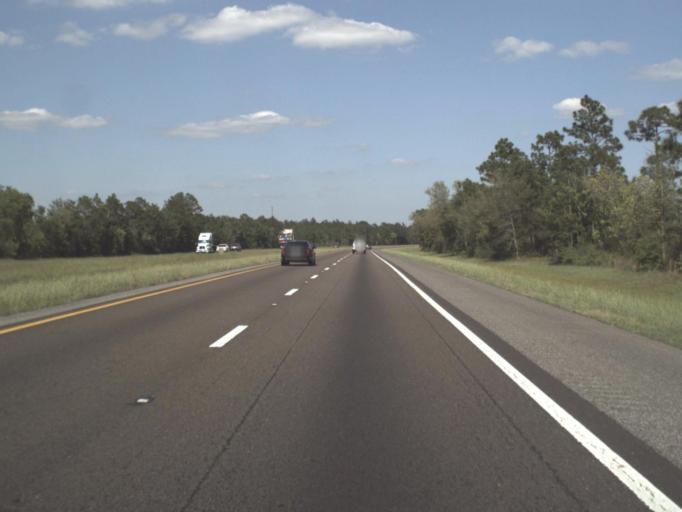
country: US
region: Florida
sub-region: Santa Rosa County
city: East Milton
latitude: 30.6680
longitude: -86.8530
